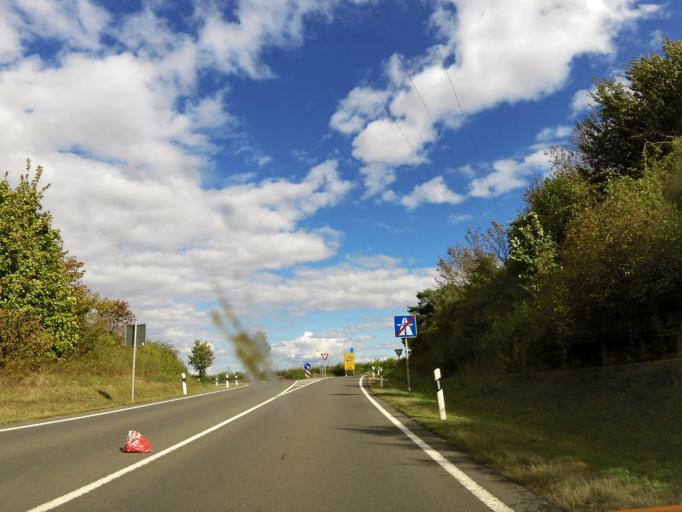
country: DE
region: Rheinland-Pfalz
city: Weitersweiler
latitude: 49.6085
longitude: 8.0026
